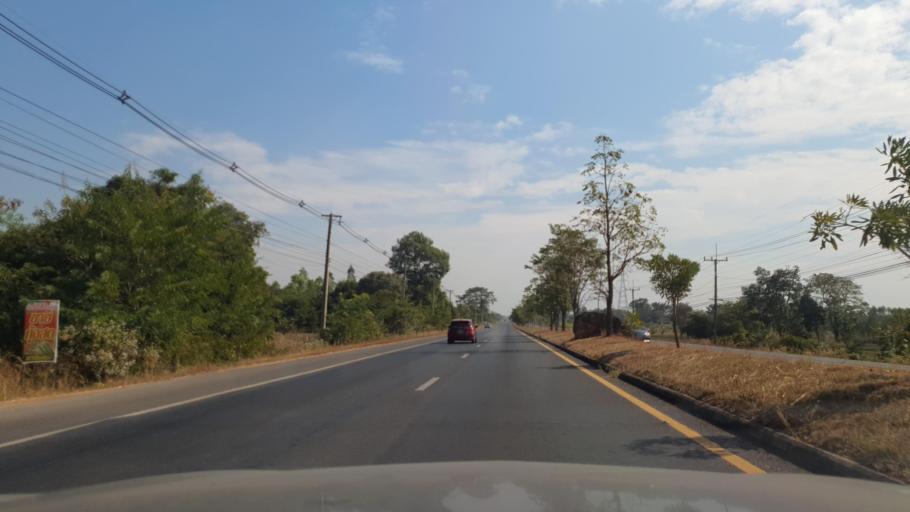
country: TH
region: Maha Sarakham
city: Kantharawichai
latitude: 16.3911
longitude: 103.2772
